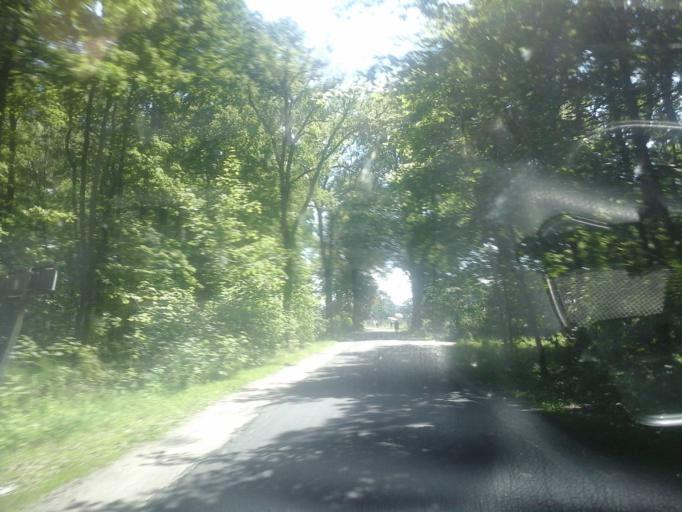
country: PL
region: West Pomeranian Voivodeship
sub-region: Powiat bialogardzki
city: Bialogard
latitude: 54.0959
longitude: 16.0534
